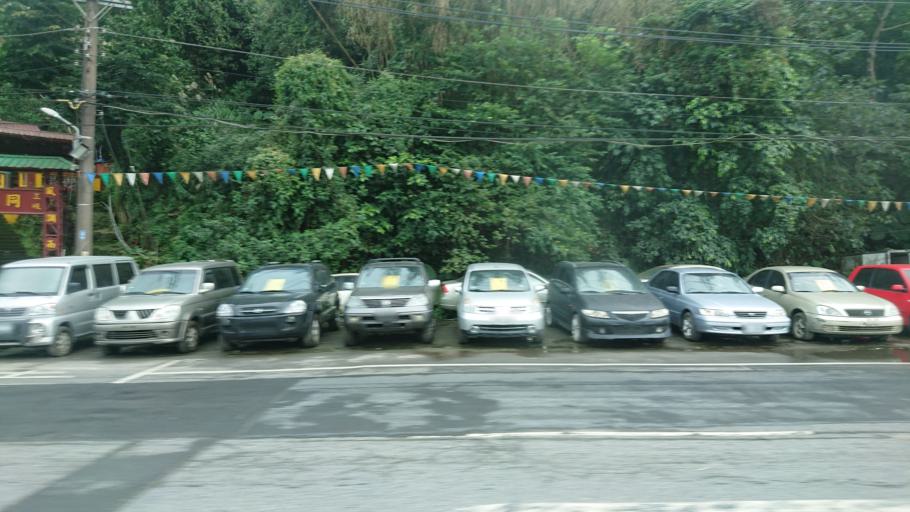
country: TW
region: Taipei
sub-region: Taipei
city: Banqiao
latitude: 24.9481
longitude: 121.4067
